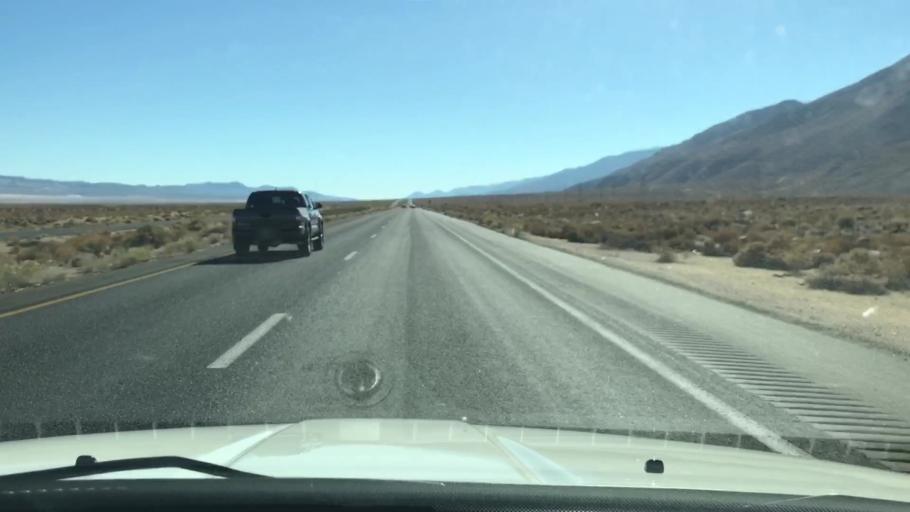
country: US
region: California
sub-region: Inyo County
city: Lone Pine
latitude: 36.4228
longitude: -118.0303
